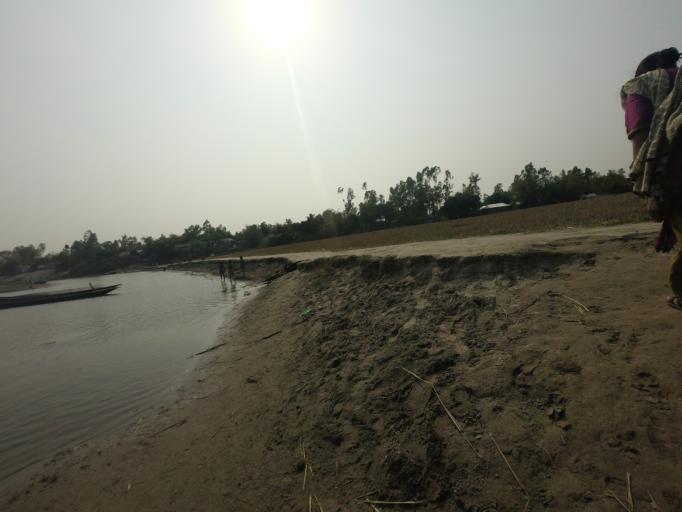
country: BD
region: Rajshahi
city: Sirajganj
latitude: 24.3336
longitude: 89.7160
